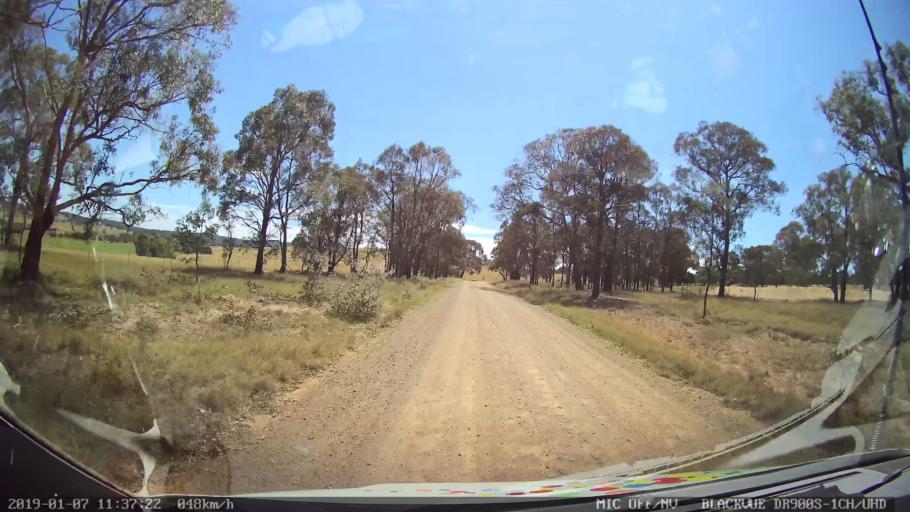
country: AU
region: New South Wales
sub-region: Armidale Dumaresq
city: Armidale
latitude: -30.3712
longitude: 151.5651
